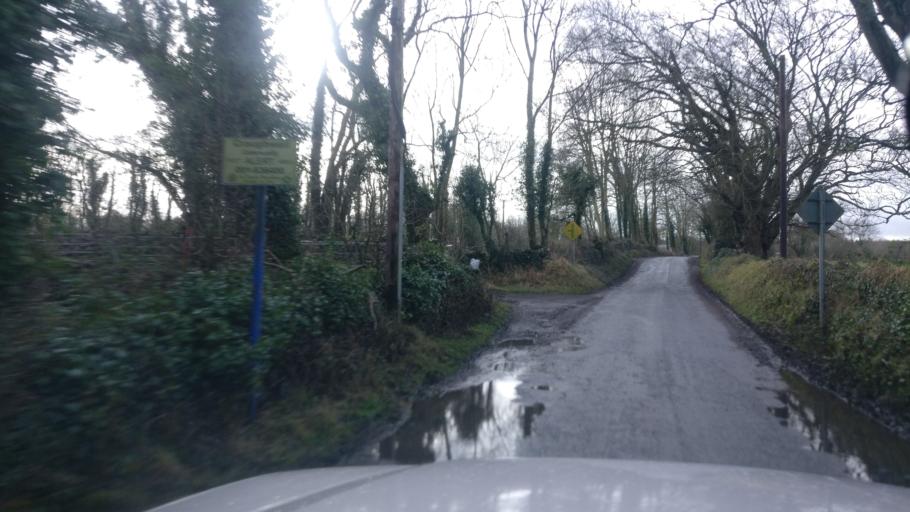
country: IE
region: Connaught
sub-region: County Galway
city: Athenry
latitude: 53.2709
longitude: -8.7726
